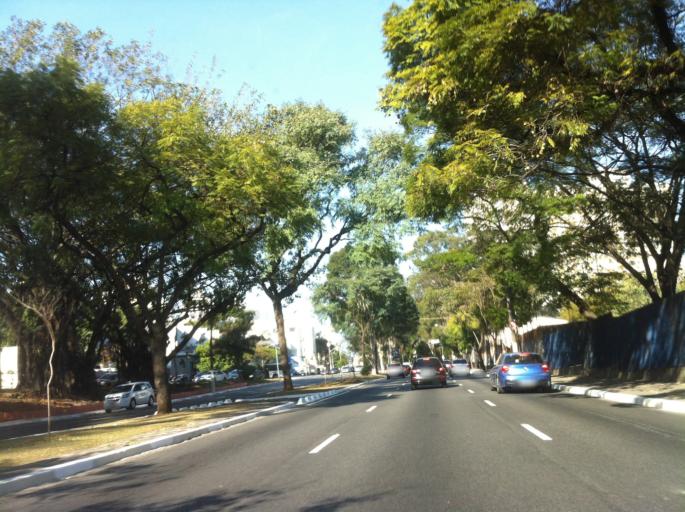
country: BR
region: Sao Paulo
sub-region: Sao Paulo
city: Sao Paulo
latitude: -23.5934
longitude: -46.6463
